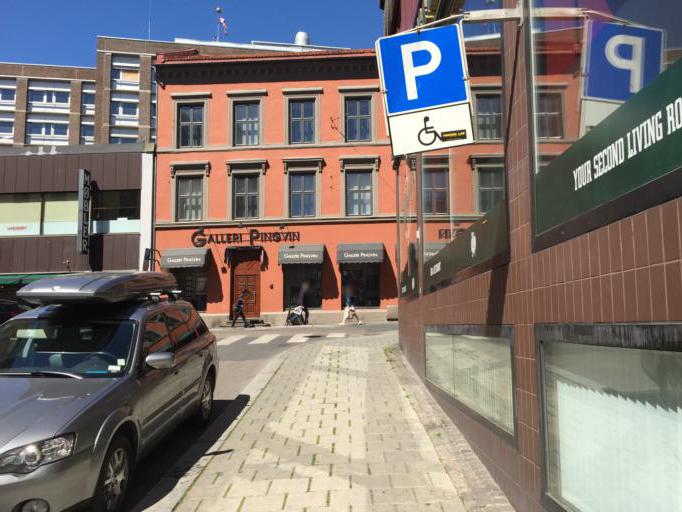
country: NO
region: Oslo
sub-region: Oslo
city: Oslo
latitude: 59.9143
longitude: 10.7470
